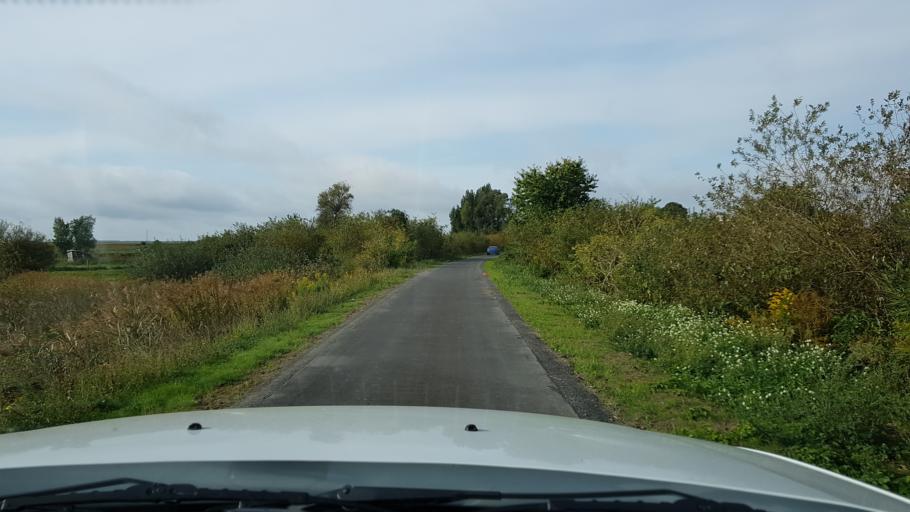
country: PL
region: West Pomeranian Voivodeship
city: Trzcinsko Zdroj
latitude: 52.9605
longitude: 14.6149
